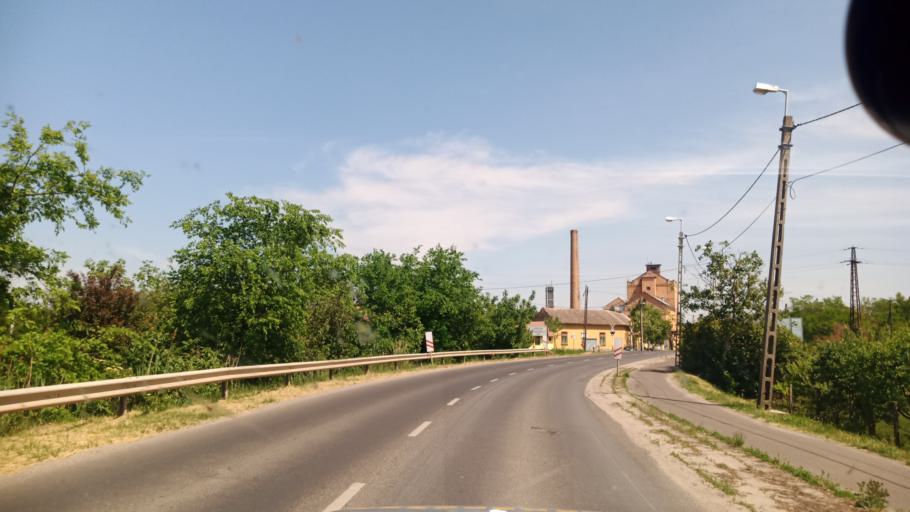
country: HU
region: Bekes
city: Oroshaza
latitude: 46.5587
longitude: 20.6507
